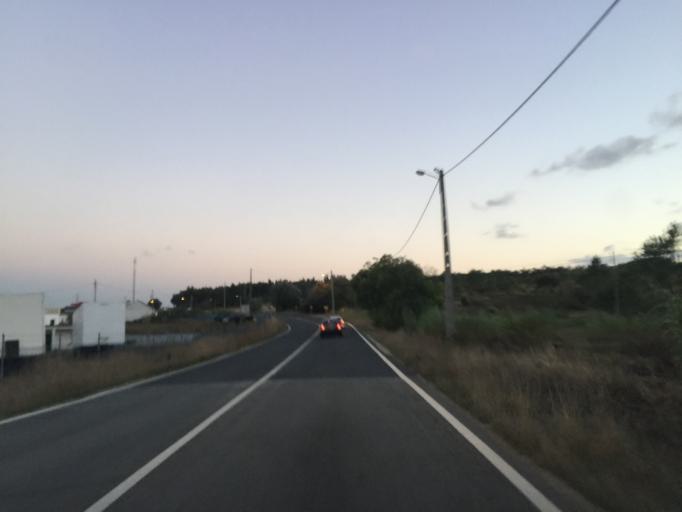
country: PT
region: Lisbon
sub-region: Alenquer
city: Alenquer
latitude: 39.1310
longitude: -8.9955
